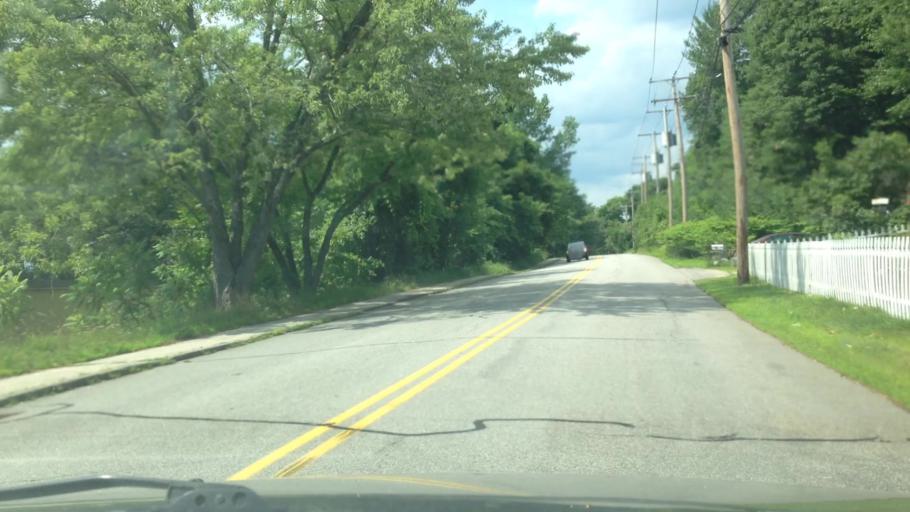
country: US
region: New Hampshire
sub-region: Cheshire County
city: Keene
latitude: 42.9231
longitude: -72.2619
